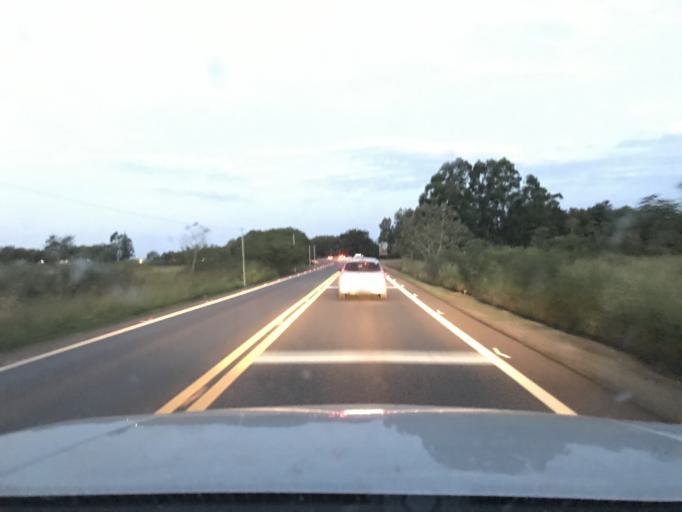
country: PY
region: Canindeyu
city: Salto del Guaira
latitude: -24.0413
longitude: -54.2775
